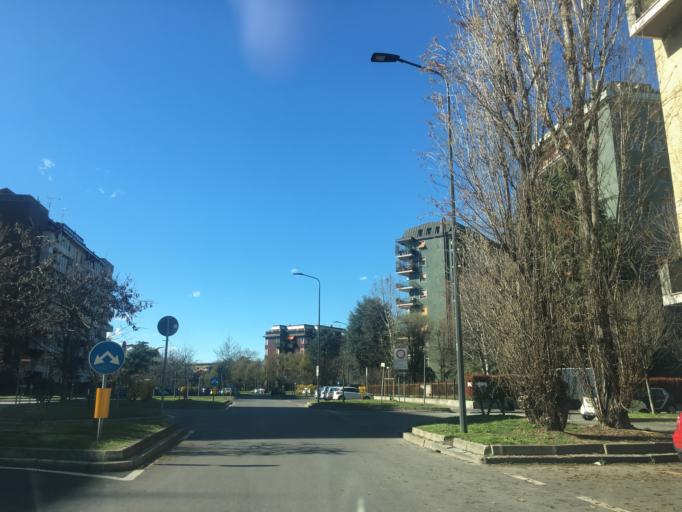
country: IT
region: Lombardy
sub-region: Citta metropolitana di Milano
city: Romano Banco
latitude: 45.4728
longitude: 9.1246
